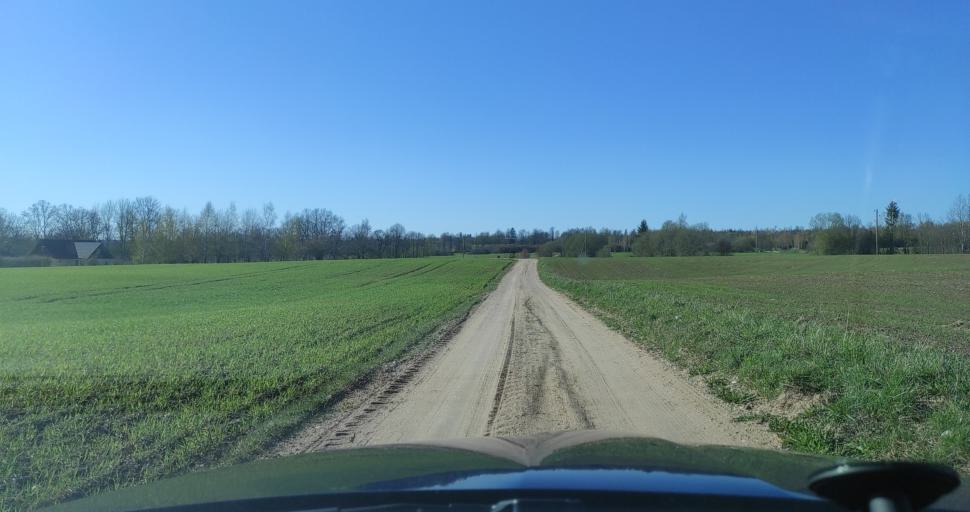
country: LV
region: Kuldigas Rajons
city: Kuldiga
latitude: 56.8725
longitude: 21.8383
